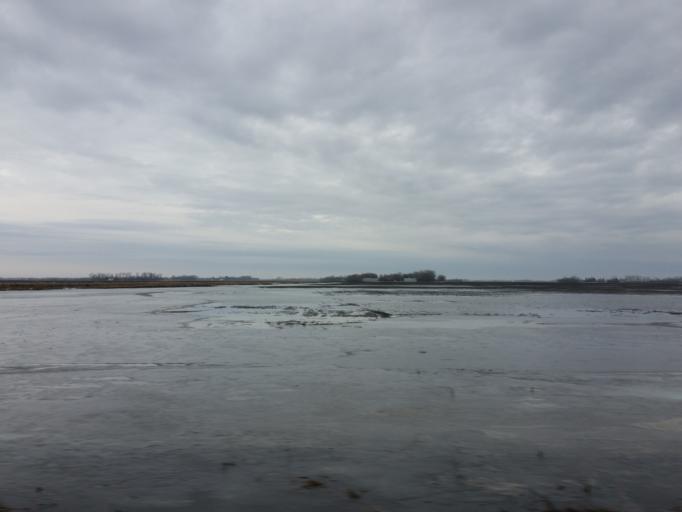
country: US
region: North Dakota
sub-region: Walsh County
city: Grafton
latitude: 48.3916
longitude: -97.4486
